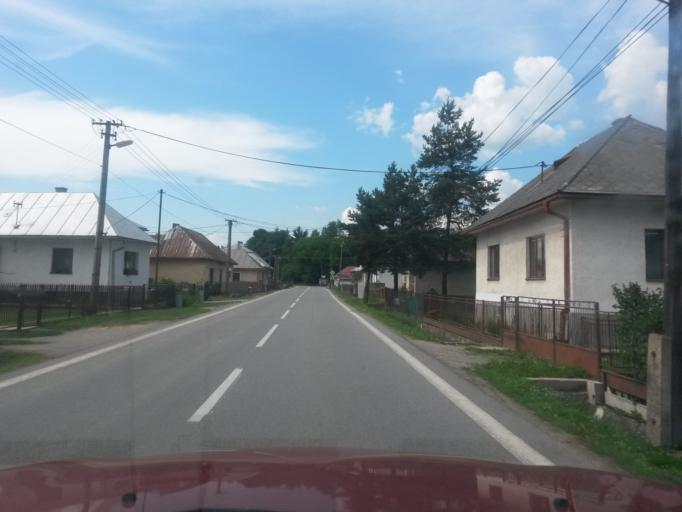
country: SK
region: Presovsky
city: Snina
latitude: 48.9951
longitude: 22.2361
